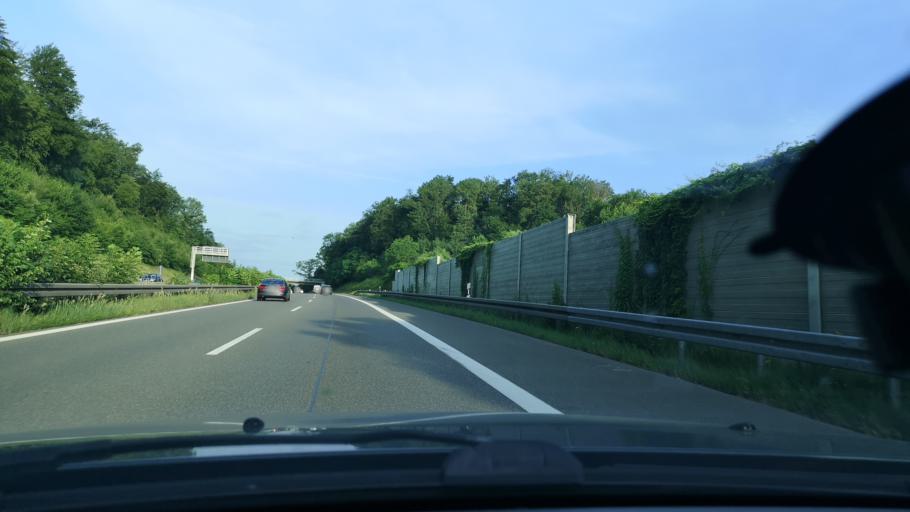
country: DE
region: Baden-Wuerttemberg
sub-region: Regierungsbezirk Stuttgart
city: Goeppingen
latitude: 48.7002
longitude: 9.6337
